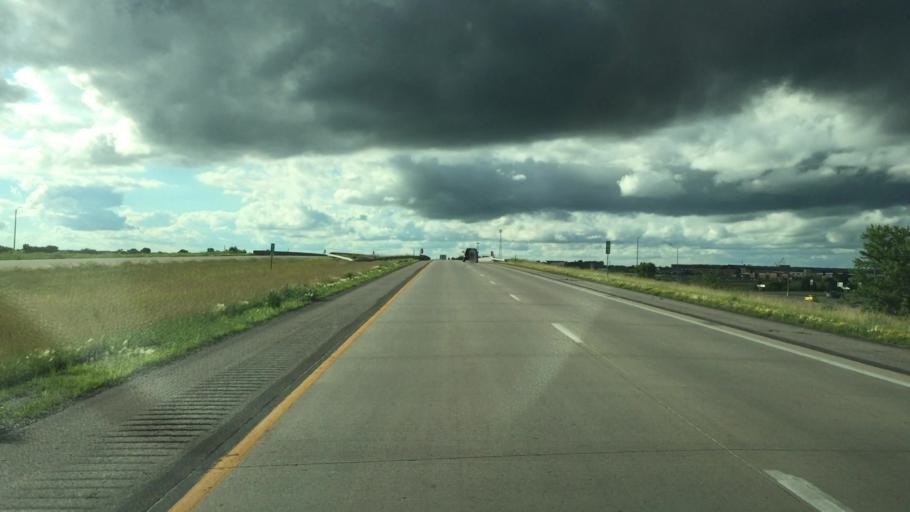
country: US
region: Iowa
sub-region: Polk County
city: Altoona
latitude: 41.6459
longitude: -93.5115
